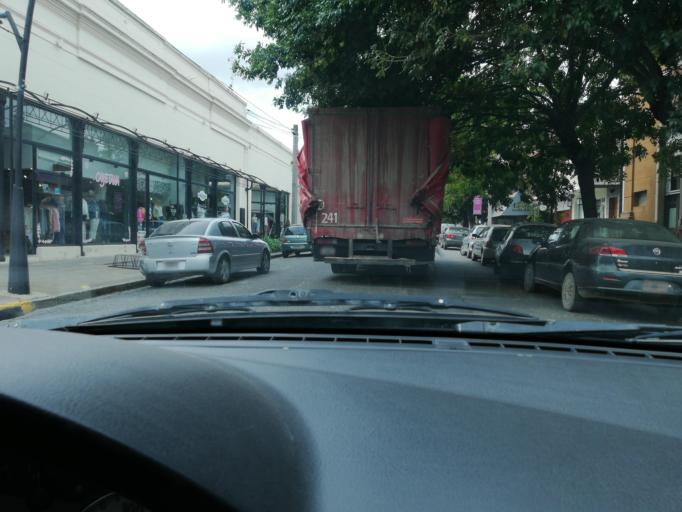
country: AR
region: Buenos Aires
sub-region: Partido de Balcarce
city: Balcarce
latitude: -37.8495
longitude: -58.2572
